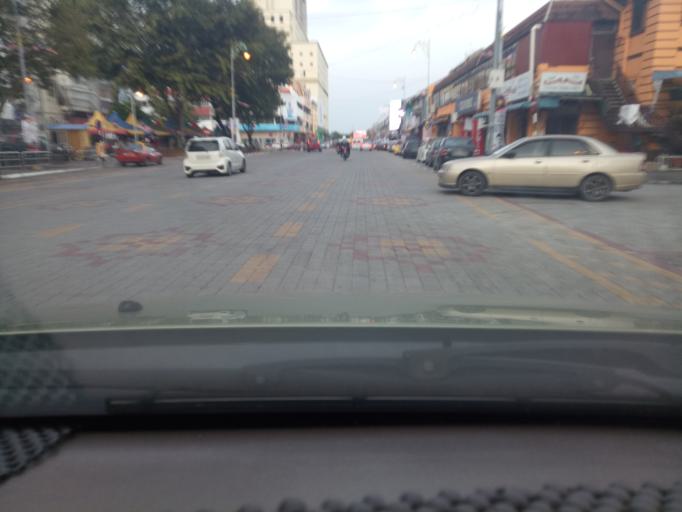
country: MY
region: Kedah
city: Alor Setar
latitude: 6.1173
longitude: 100.3677
